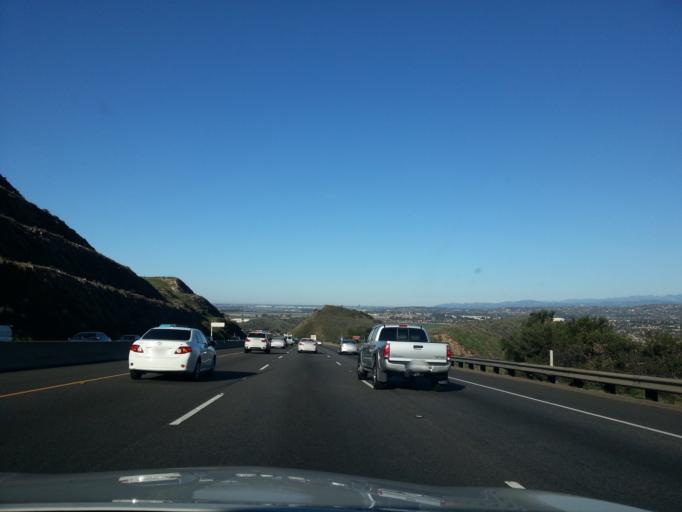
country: US
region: California
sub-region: Ventura County
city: Casa Conejo
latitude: 34.2012
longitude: -118.9677
